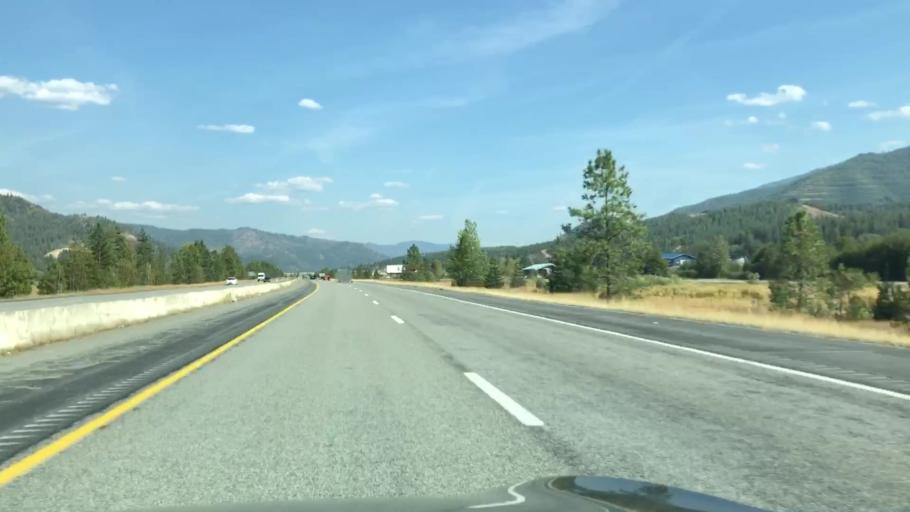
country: US
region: Idaho
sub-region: Shoshone County
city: Pinehurst
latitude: 47.5466
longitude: -116.2077
